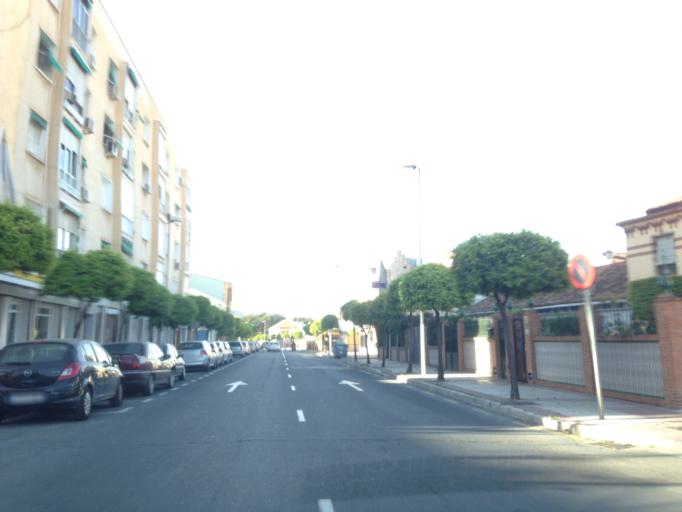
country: ES
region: Andalusia
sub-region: Provincia de Malaga
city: Malaga
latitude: 36.7364
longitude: -4.4233
